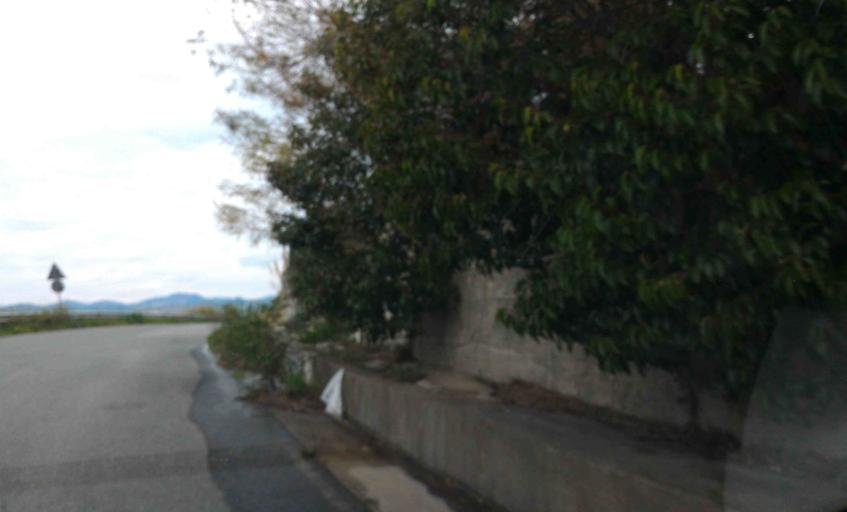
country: IT
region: Calabria
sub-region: Provincia di Catanzaro
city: Sellia Marina
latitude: 38.8858
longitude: 16.7115
